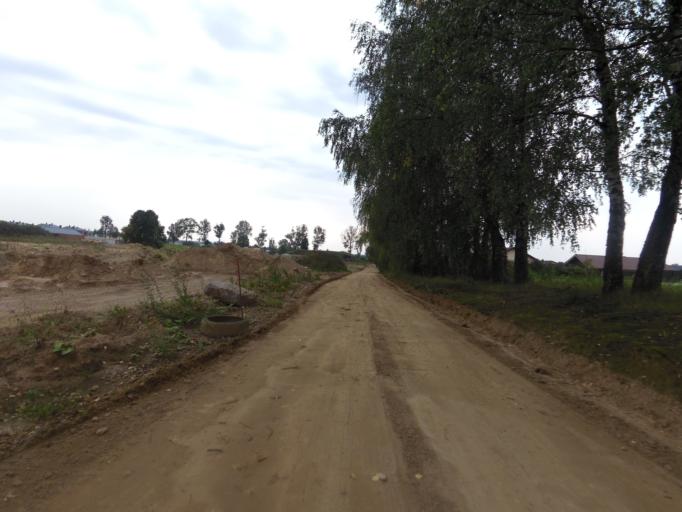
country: LT
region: Vilnius County
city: Pilaite
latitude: 54.7239
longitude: 25.1481
